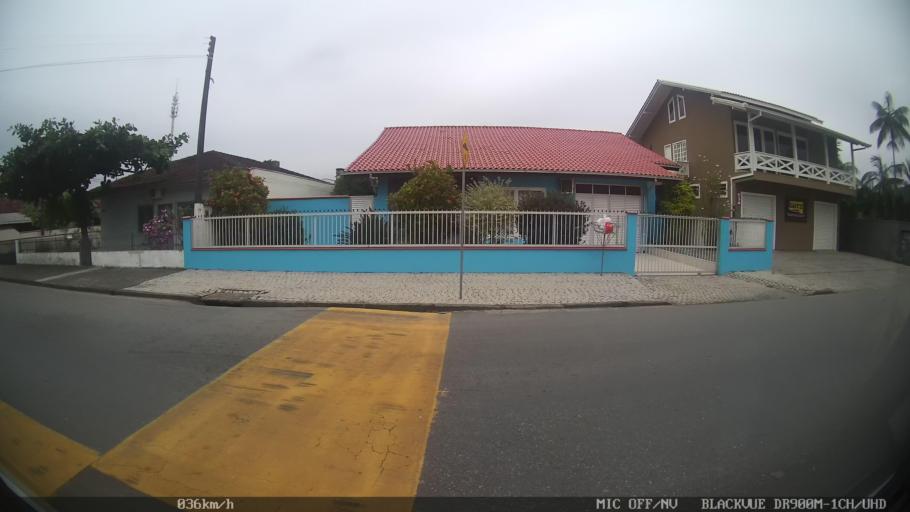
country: BR
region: Santa Catarina
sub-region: Joinville
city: Joinville
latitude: -26.2671
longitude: -48.8180
